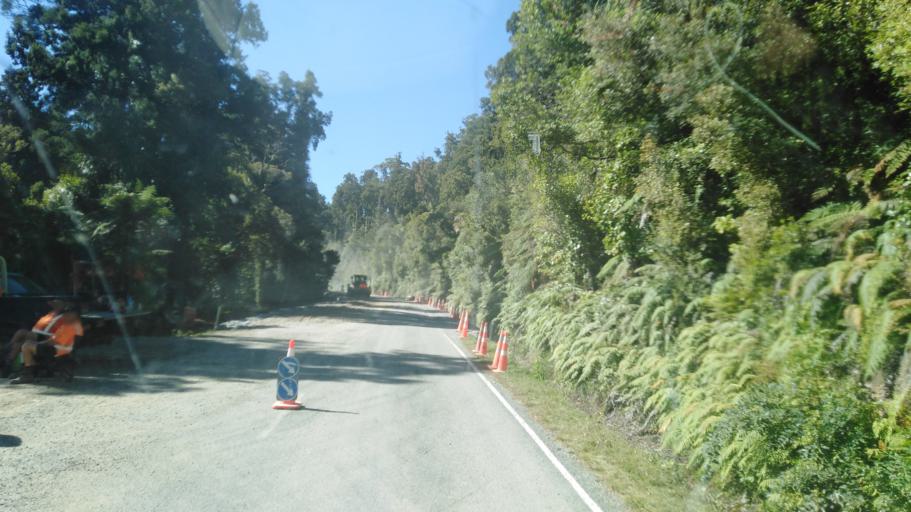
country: NZ
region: West Coast
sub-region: Buller District
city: Westport
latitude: -41.5279
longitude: 172.0033
